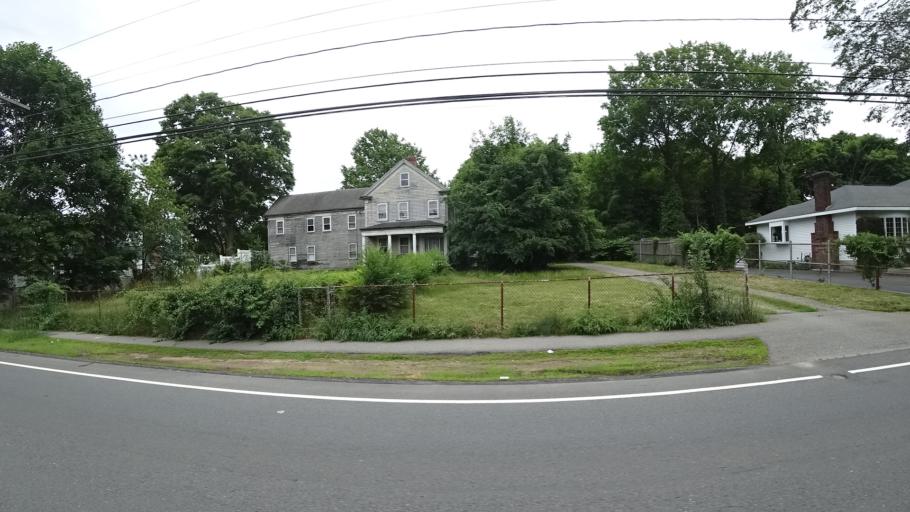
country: US
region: Massachusetts
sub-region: Norfolk County
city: Dedham
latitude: 42.2333
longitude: -71.1566
